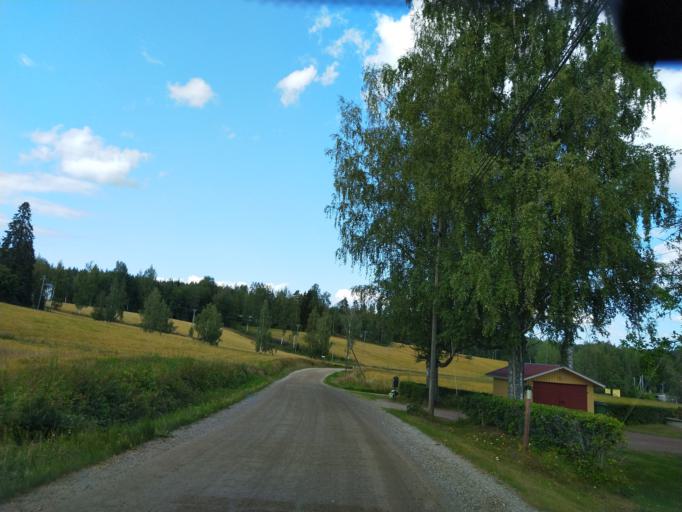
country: FI
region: Pirkanmaa
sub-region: Ylae-Pirkanmaa
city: Ruovesi
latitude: 61.9600
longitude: 24.0350
